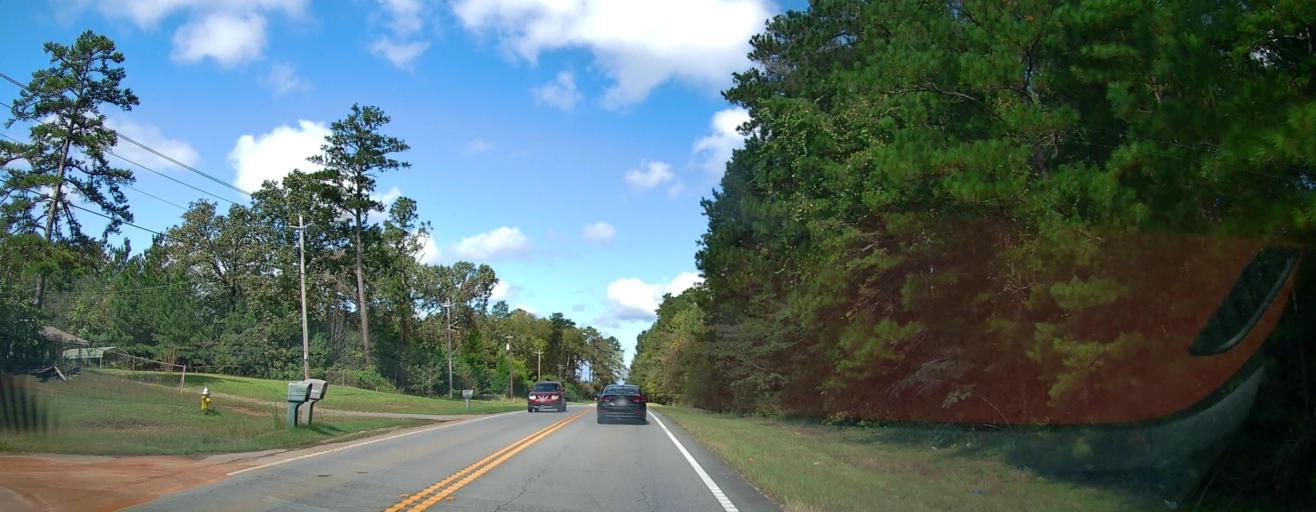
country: US
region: Georgia
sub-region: Bibb County
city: Macon
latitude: 32.8305
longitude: -83.5738
